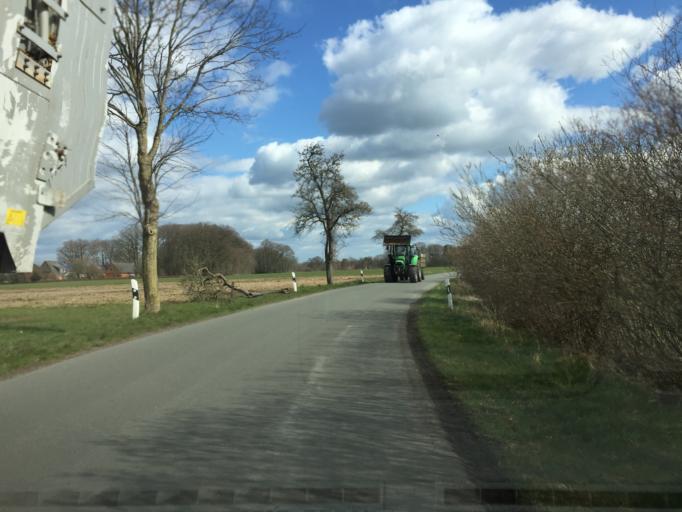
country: DE
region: Lower Saxony
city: Engeln
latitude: 52.7598
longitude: 8.9378
